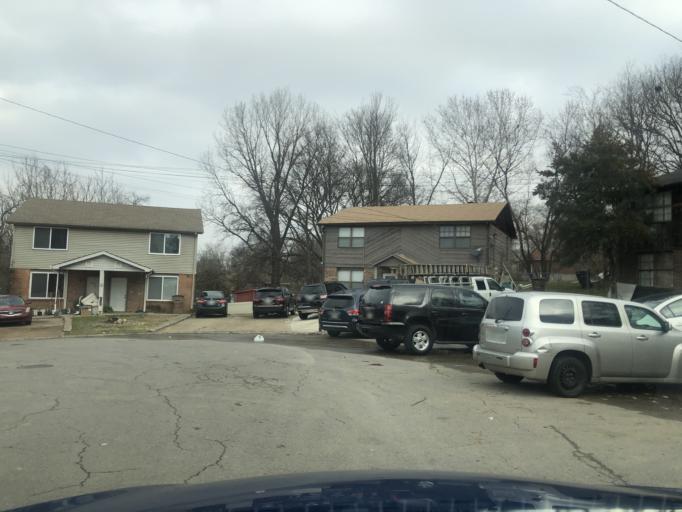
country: US
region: Tennessee
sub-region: Davidson County
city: Oak Hill
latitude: 36.0939
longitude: -86.7122
